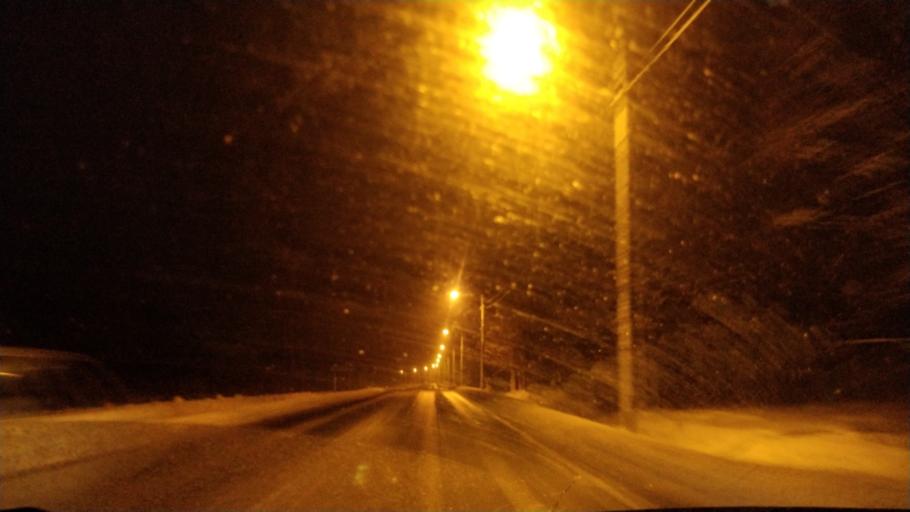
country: FI
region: Lapland
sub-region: Rovaniemi
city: Rovaniemi
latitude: 66.4073
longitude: 25.3976
